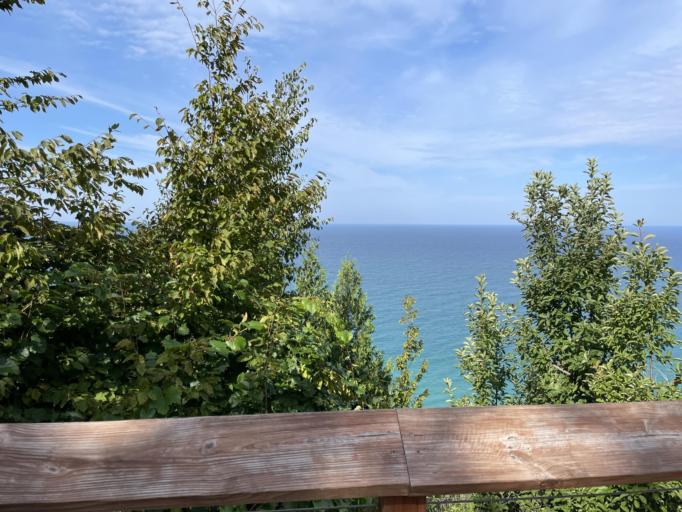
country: US
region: Michigan
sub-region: Benzie County
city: Frankfort
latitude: 44.5276
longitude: -86.2303
